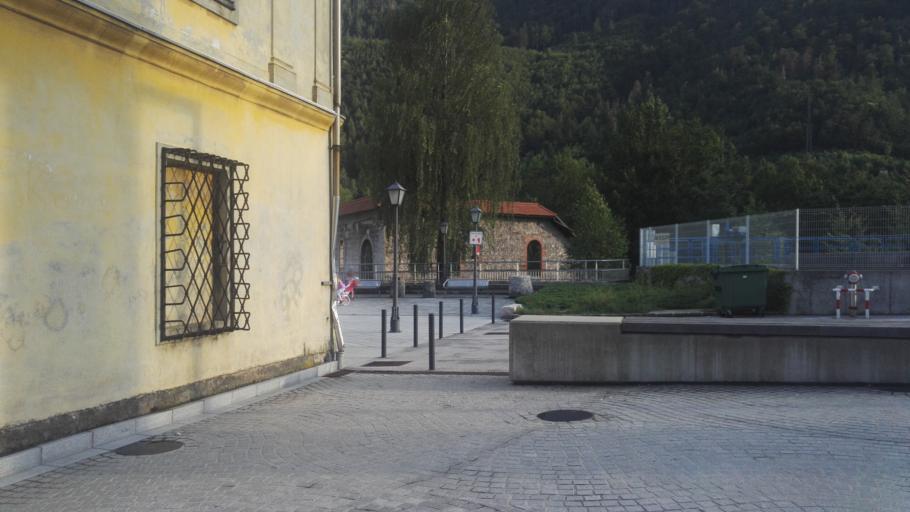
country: SI
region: Jesenice
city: Jesenice
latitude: 46.4332
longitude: 14.0570
